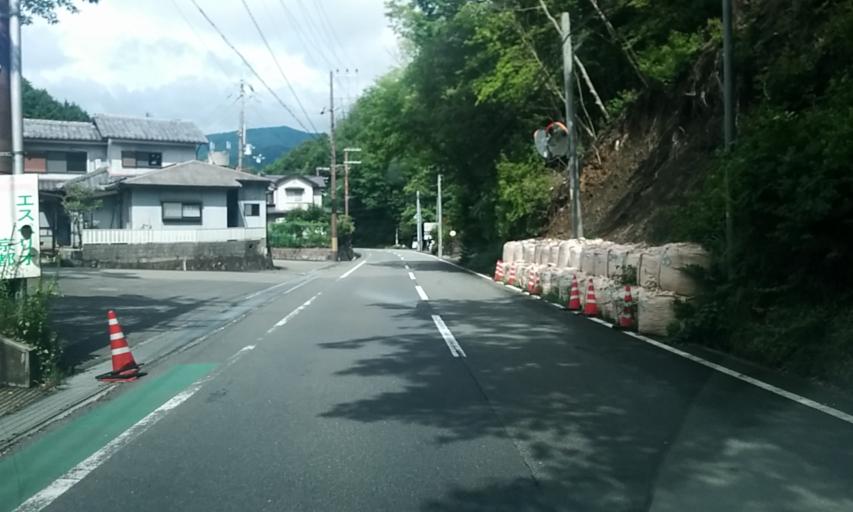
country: JP
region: Kyoto
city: Kameoka
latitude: 35.0202
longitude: 135.5114
